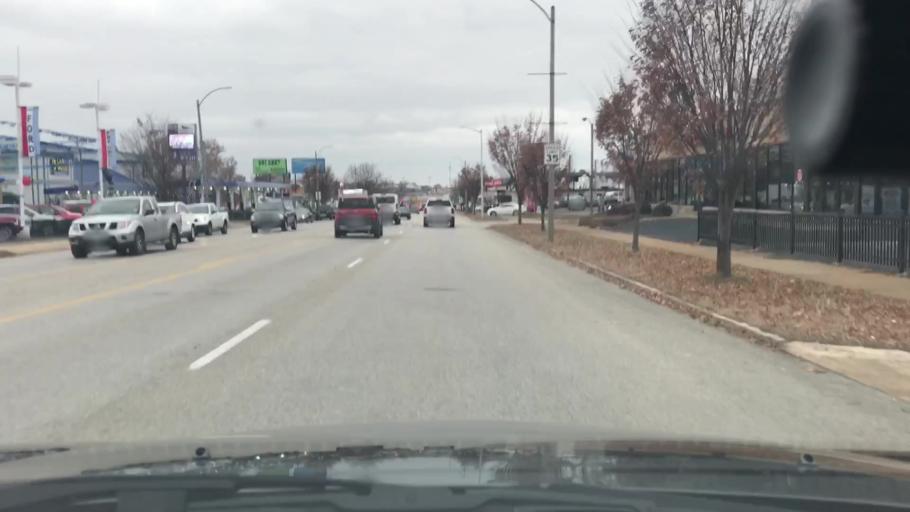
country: US
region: Missouri
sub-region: Saint Louis County
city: Maplewood
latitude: 38.5982
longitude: -90.2706
